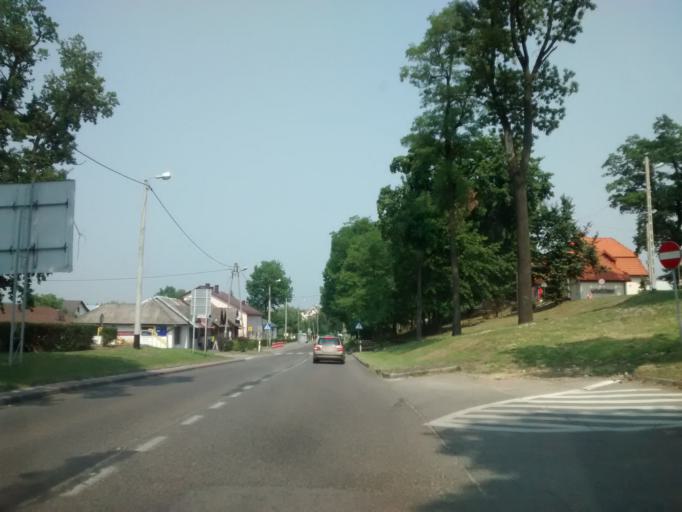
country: PL
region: Lesser Poland Voivodeship
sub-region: Powiat olkuski
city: Klucze
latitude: 50.3371
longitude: 19.5621
